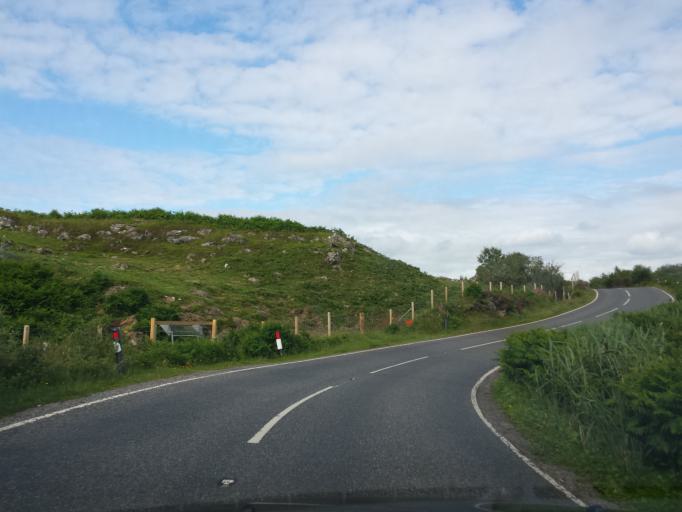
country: GB
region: Scotland
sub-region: Argyll and Bute
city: Isle Of Mull
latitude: 56.9627
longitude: -5.8339
